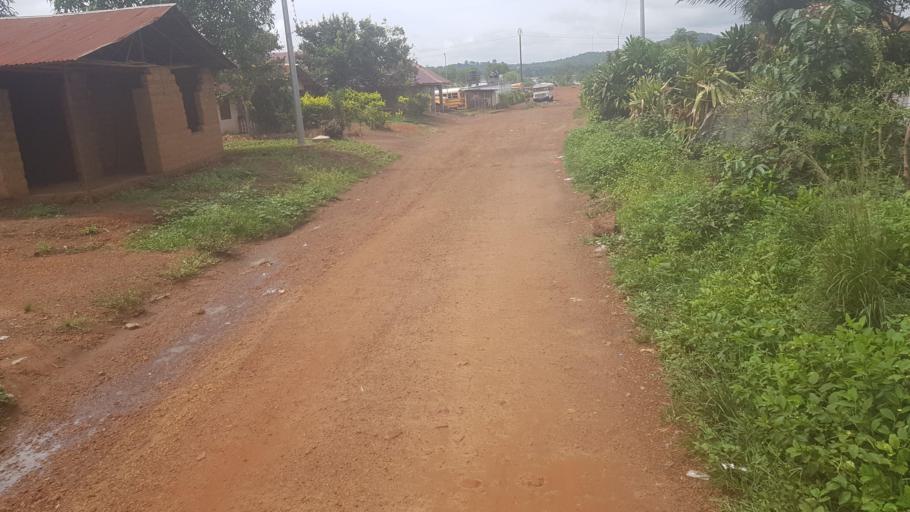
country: SL
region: Southern Province
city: Mogbwemo
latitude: 7.7584
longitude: -12.3052
